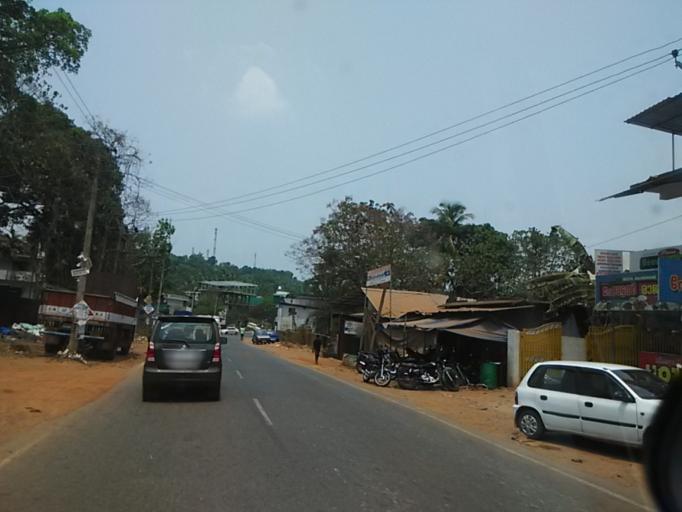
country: IN
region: Kerala
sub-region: Kannur
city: Mattanur
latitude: 11.9788
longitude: 75.6696
